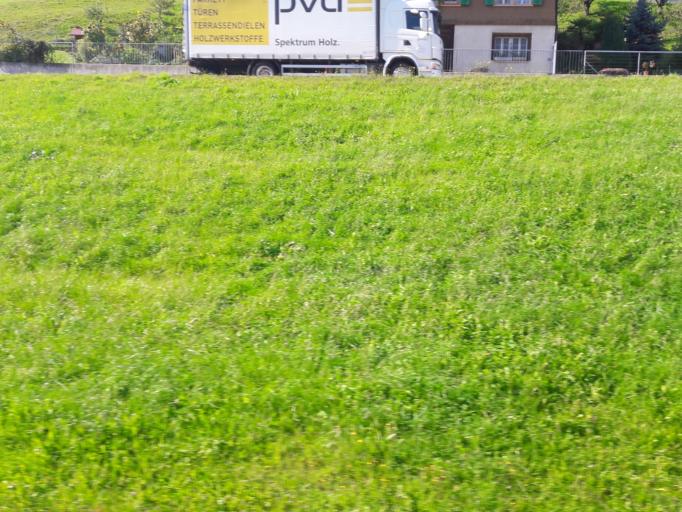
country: CH
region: Schwyz
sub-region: Bezirk Schwyz
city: Sattel
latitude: 47.0744
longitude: 8.6237
